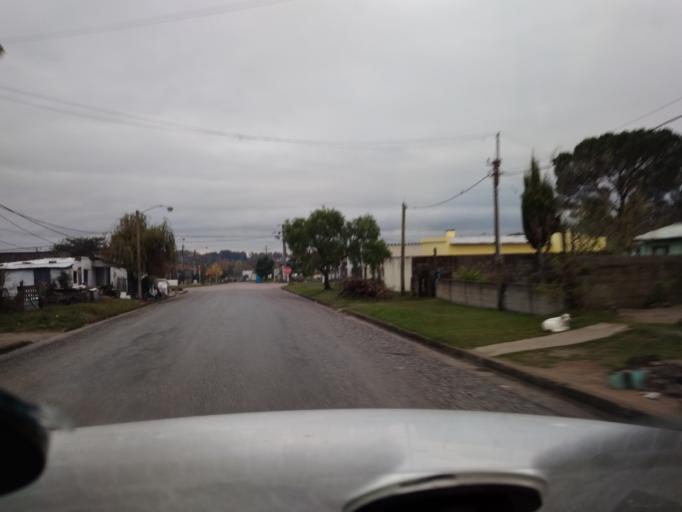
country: UY
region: Florida
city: Florida
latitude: -34.1071
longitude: -56.2074
